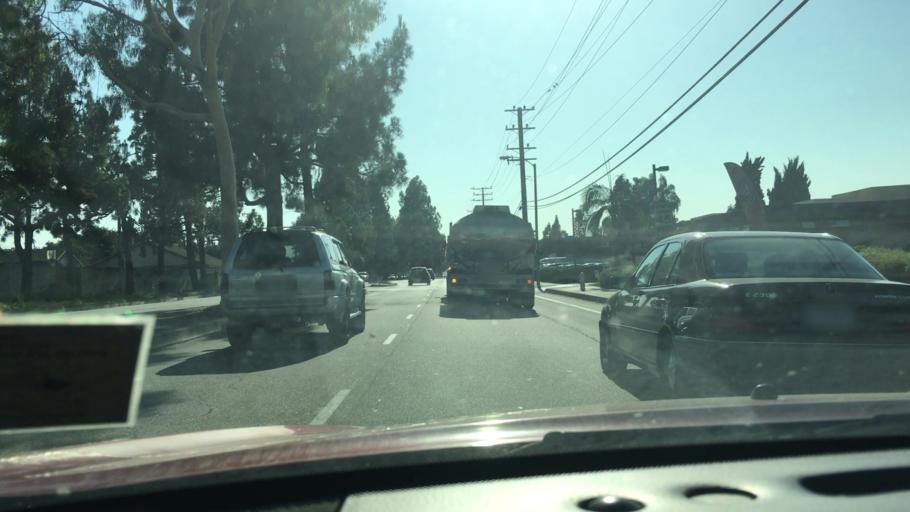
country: US
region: California
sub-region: Los Angeles County
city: Cerritos
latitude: 33.8733
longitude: -118.0472
